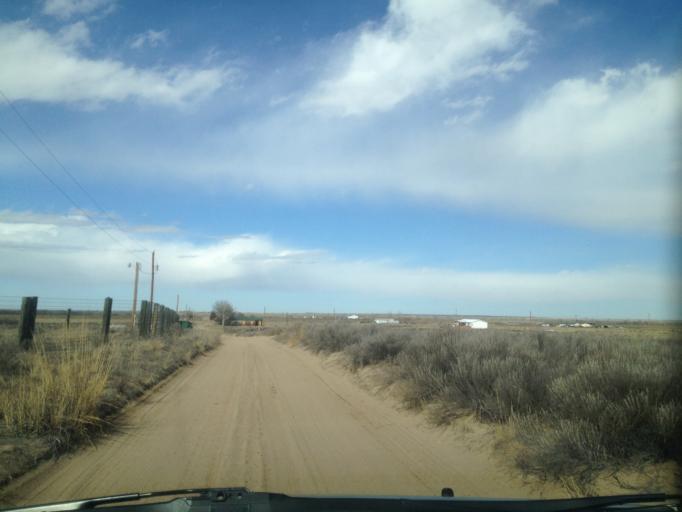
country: US
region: Colorado
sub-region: Weld County
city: Keenesburg
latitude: 40.2848
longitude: -104.2591
